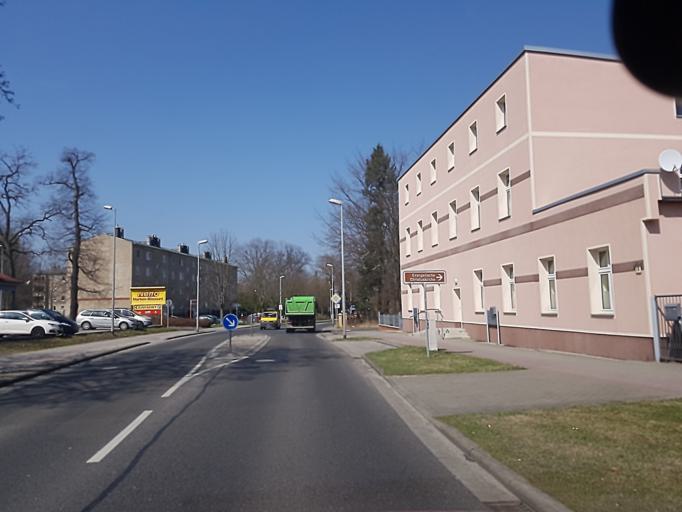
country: DE
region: Brandenburg
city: Tschernitz
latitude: 51.6166
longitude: 14.5948
